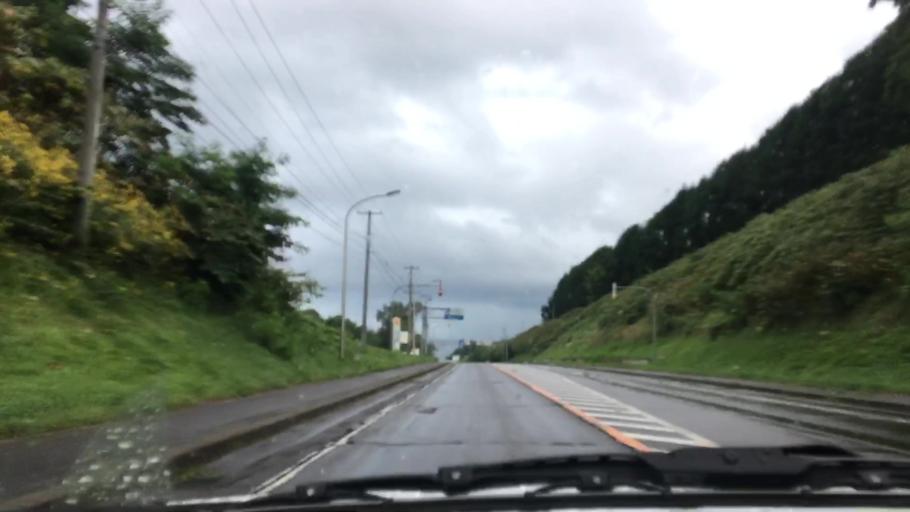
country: JP
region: Hokkaido
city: Nanae
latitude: 42.1002
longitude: 140.5664
